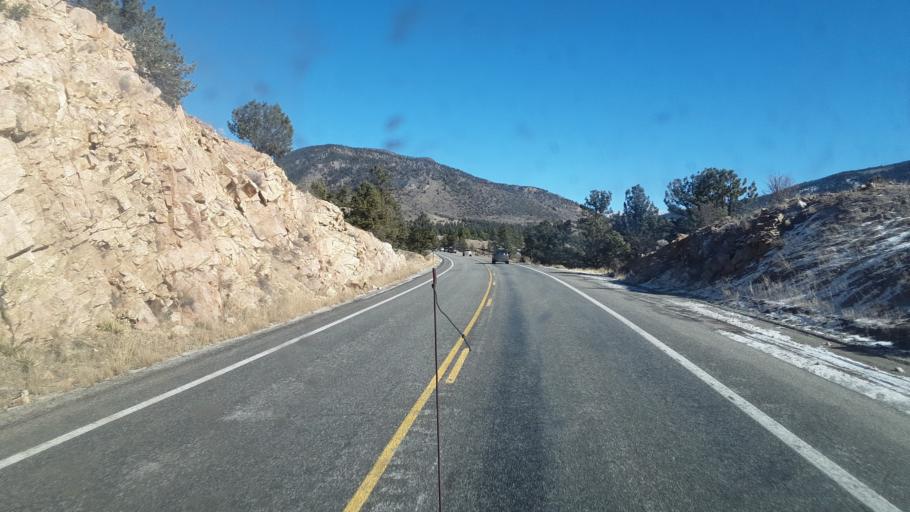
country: US
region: Colorado
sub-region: Chaffee County
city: Buena Vista
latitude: 38.8437
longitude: -105.9913
